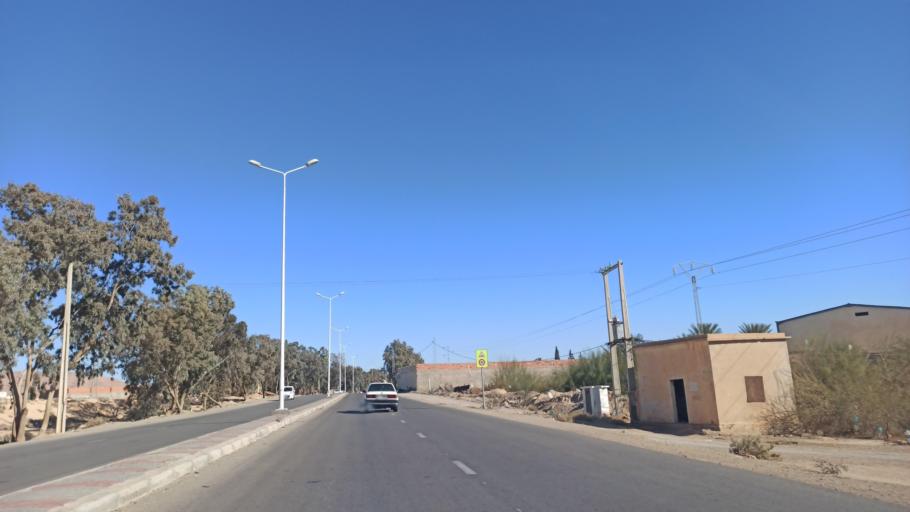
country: TN
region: Gafsa
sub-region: Gafsa Municipality
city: Gafsa
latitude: 34.3995
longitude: 8.7221
